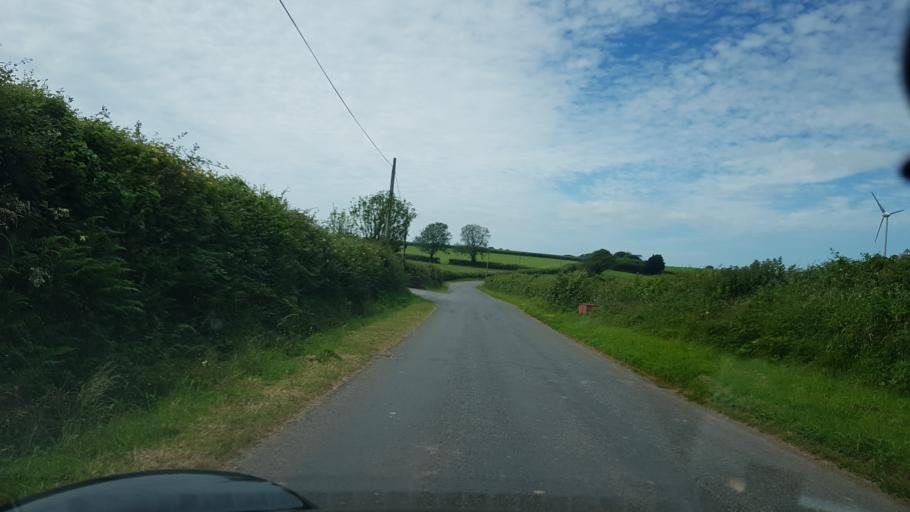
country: GB
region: Wales
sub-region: Carmarthenshire
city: Llanddowror
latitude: 51.7679
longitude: -4.5192
